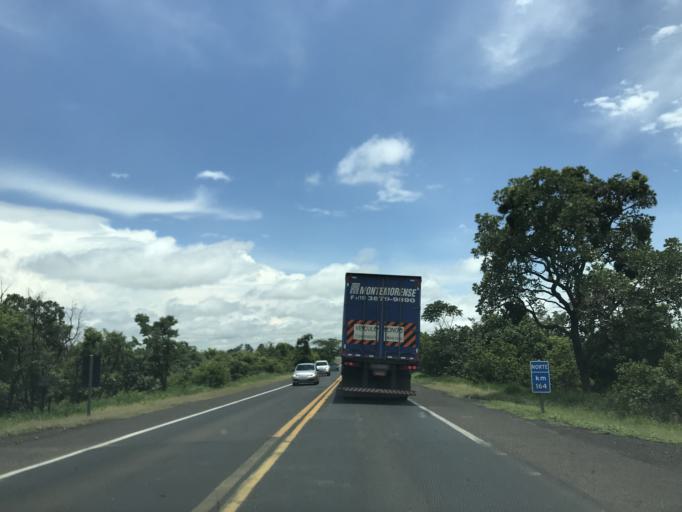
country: BR
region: Minas Gerais
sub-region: Prata
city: Prata
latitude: -19.6578
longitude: -48.9780
